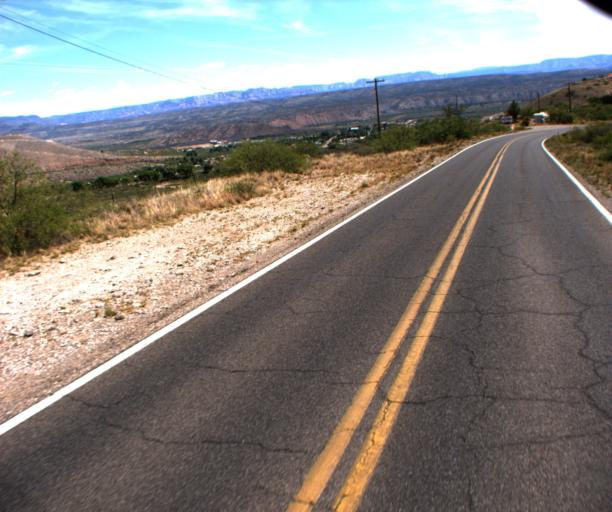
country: US
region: Arizona
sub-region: Yavapai County
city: Clarkdale
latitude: 34.7599
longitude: -112.0797
